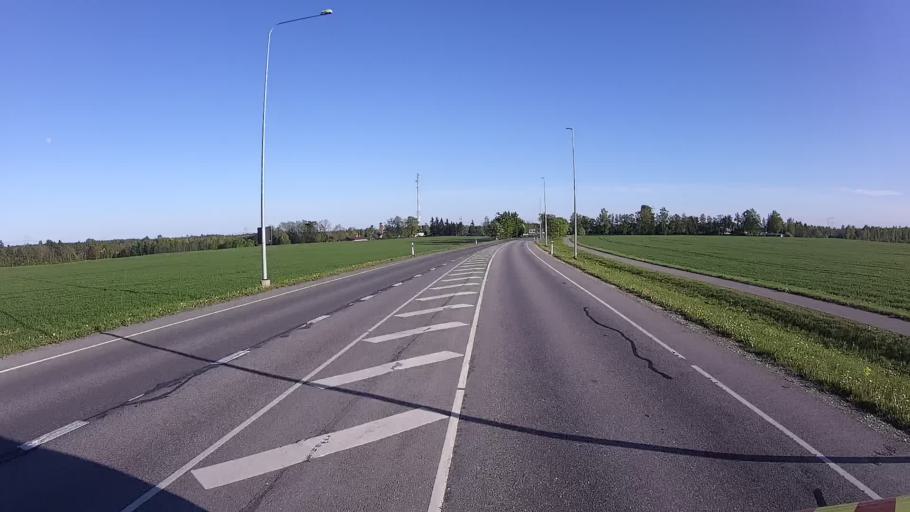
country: EE
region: Viljandimaa
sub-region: Viljandi linn
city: Viljandi
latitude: 58.3892
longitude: 25.5944
